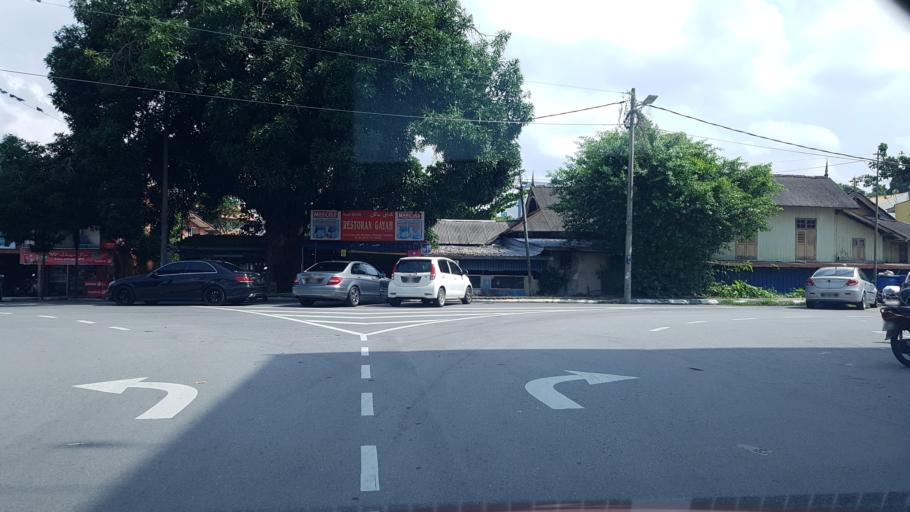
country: MY
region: Terengganu
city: Kuala Terengganu
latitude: 5.3285
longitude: 103.1369
